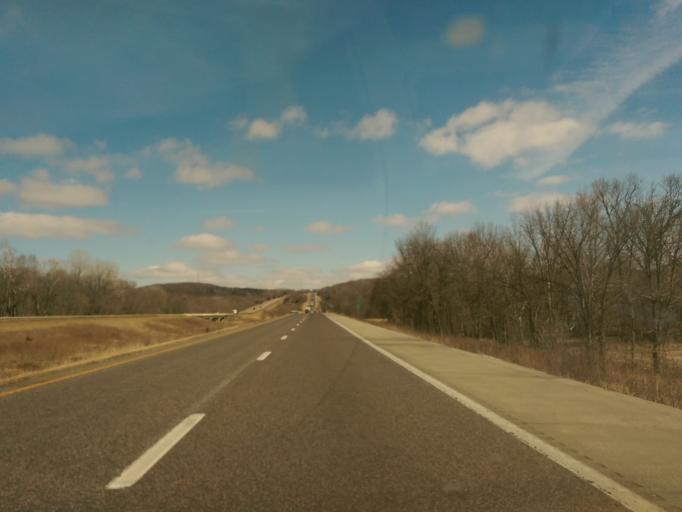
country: US
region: Missouri
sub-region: Montgomery County
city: Montgomery City
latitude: 38.8994
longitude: -91.5862
